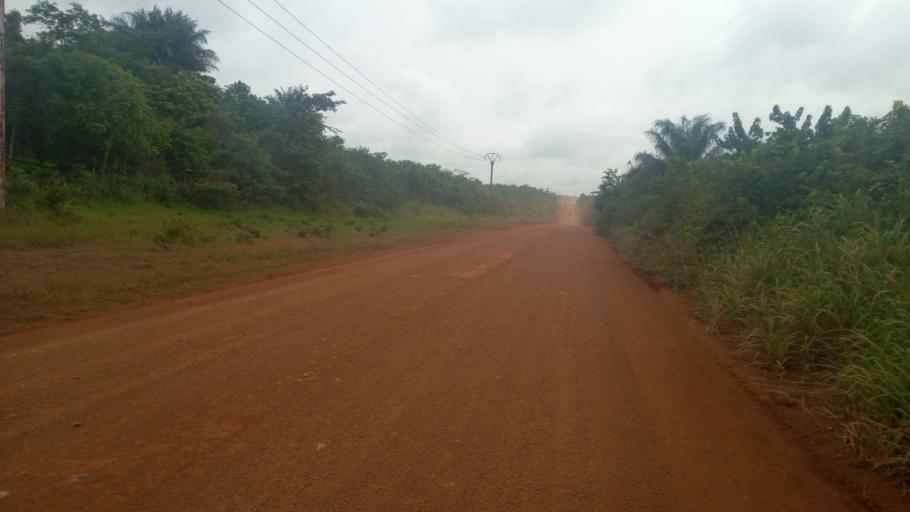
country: SL
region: Southern Province
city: Mogbwemo
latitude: 7.7085
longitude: -12.2847
